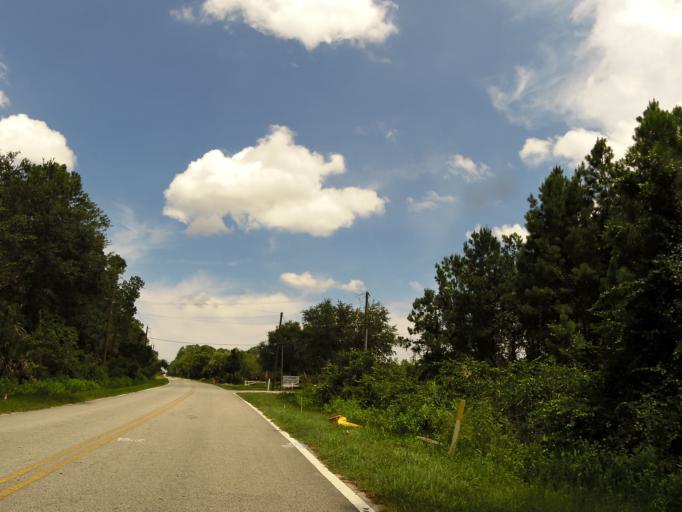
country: US
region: Florida
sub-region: Flagler County
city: Flagler Beach
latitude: 29.4035
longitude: -81.1826
